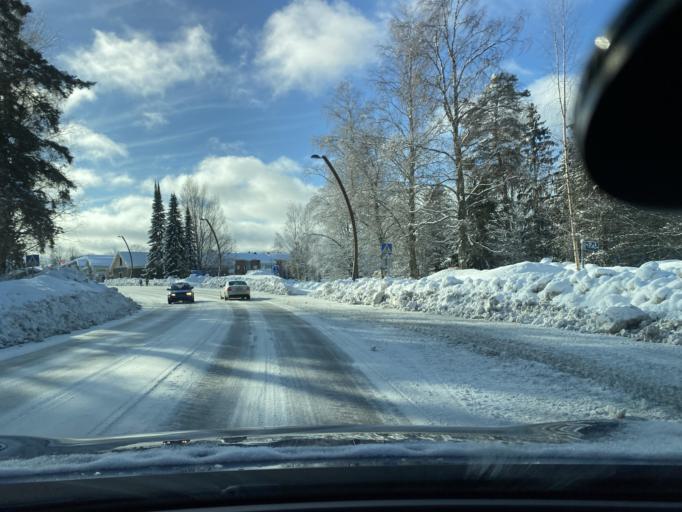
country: FI
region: Southern Savonia
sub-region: Mikkeli
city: Kangasniemi
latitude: 61.9916
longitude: 26.6438
